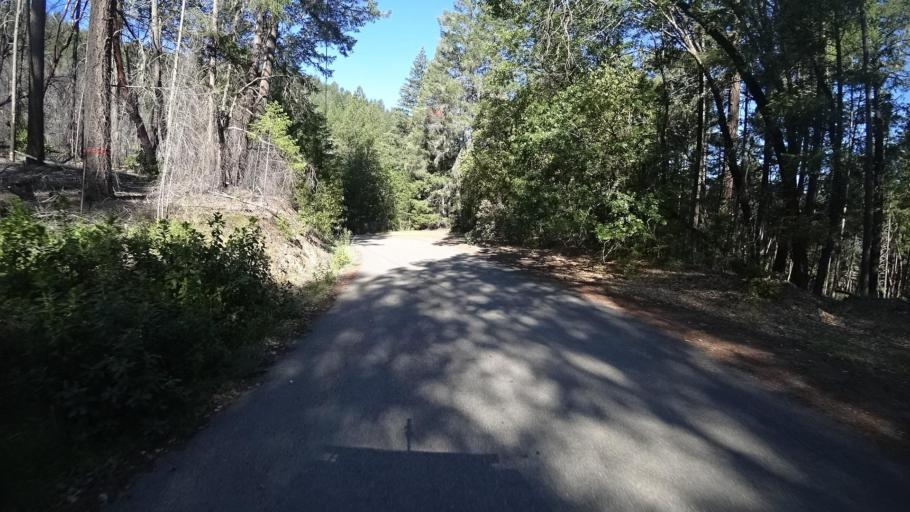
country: US
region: California
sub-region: Lake County
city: Upper Lake
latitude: 39.4039
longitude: -122.9686
